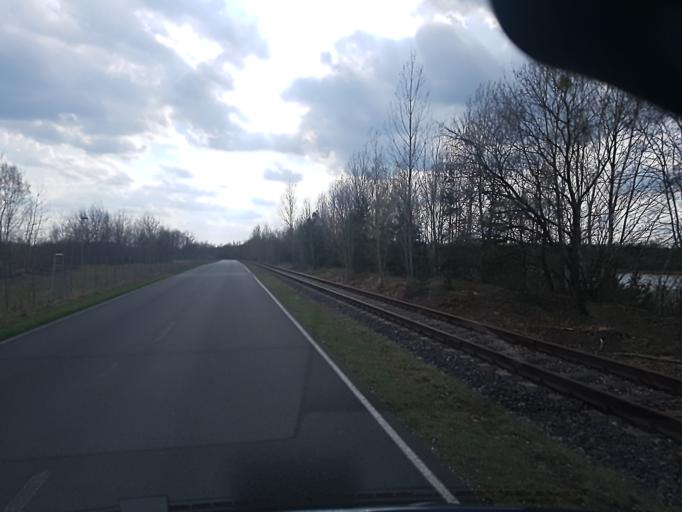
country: DE
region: Saxony-Anhalt
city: Grafenhainichen
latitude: 51.7561
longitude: 12.4407
